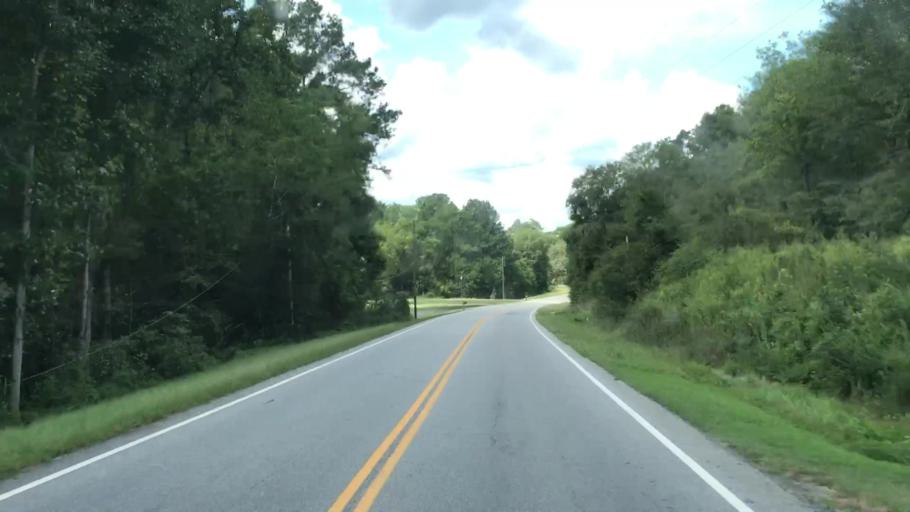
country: US
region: Georgia
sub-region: Greene County
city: Greensboro
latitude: 33.6407
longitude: -83.2246
